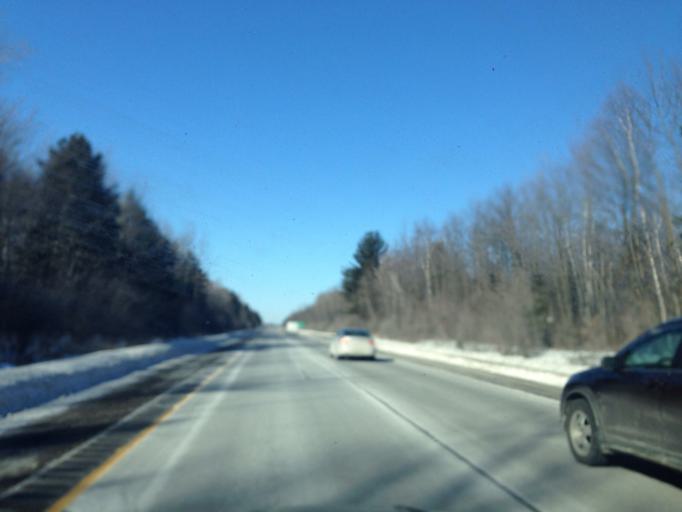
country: CA
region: Ontario
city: Ottawa
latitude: 45.3638
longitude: -75.4957
